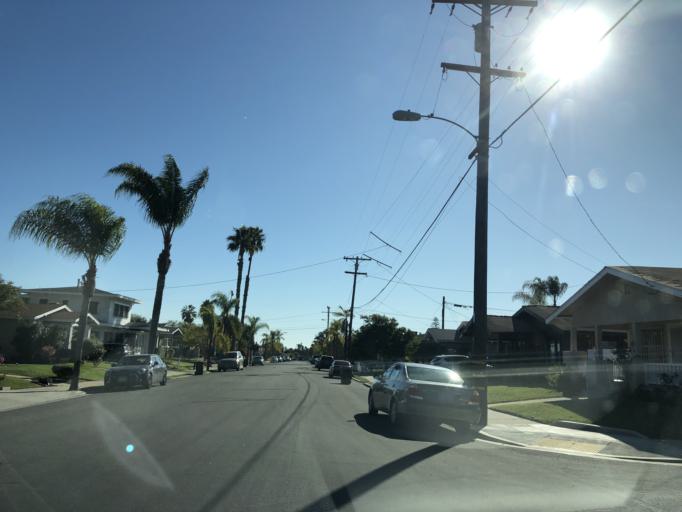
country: US
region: California
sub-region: San Diego County
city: San Diego
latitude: 32.7385
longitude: -117.1304
